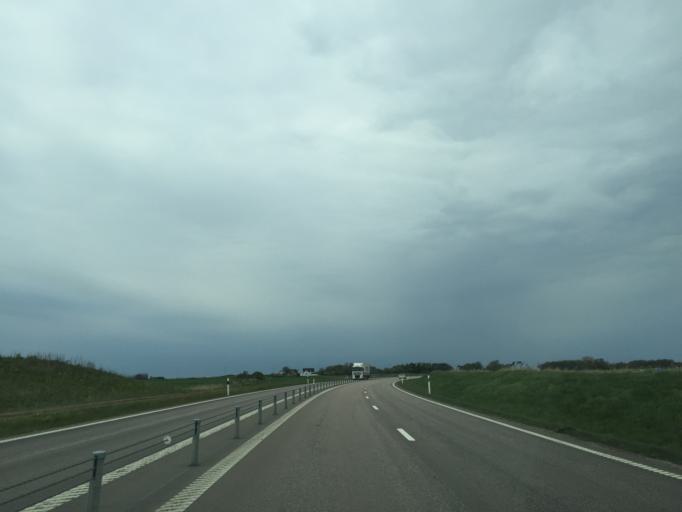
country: SE
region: Skane
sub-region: Hoganas Kommun
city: Hoganas
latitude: 56.1653
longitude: 12.5774
